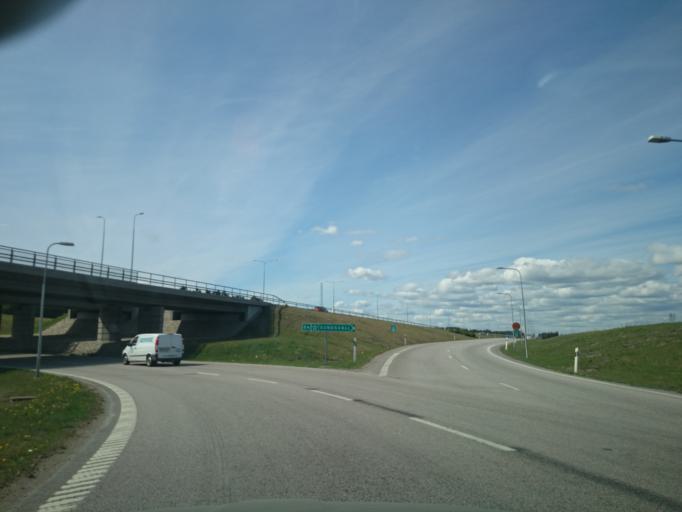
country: SE
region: Uppsala
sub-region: Uppsala Kommun
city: Gamla Uppsala
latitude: 59.8885
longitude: 17.6700
